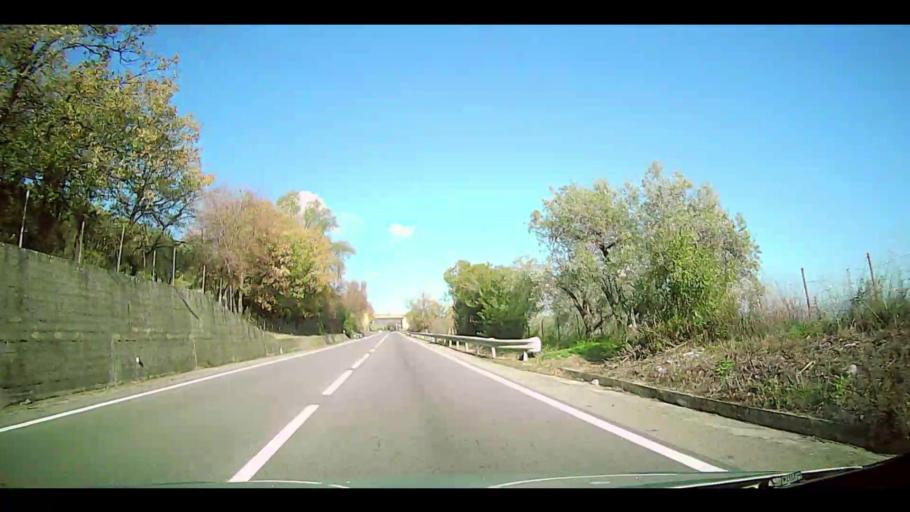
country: IT
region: Calabria
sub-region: Provincia di Crotone
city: Caccuri
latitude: 39.2052
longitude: 16.8059
